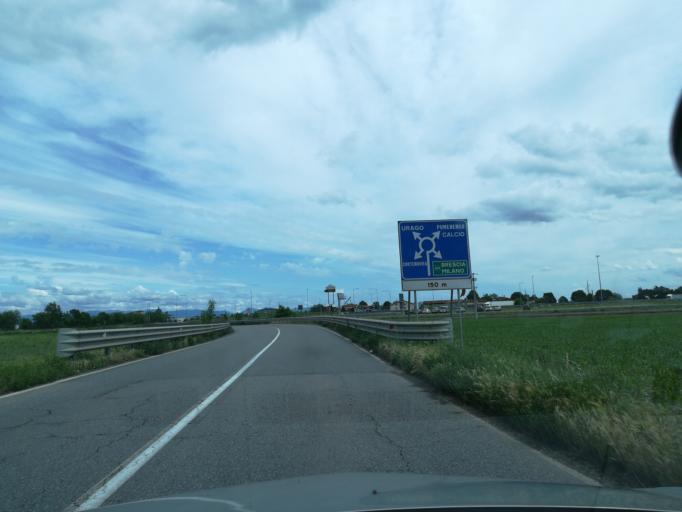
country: IT
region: Lombardy
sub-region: Provincia di Bergamo
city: Calcio
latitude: 45.4995
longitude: 9.8274
